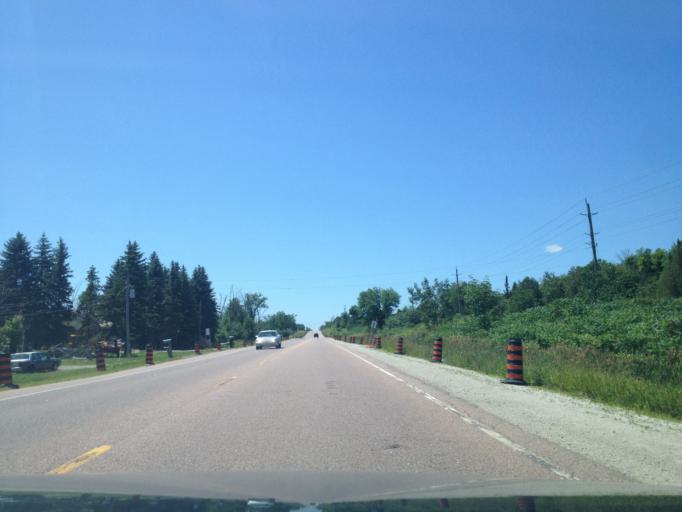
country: CA
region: Ontario
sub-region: Halton
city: Milton
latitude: 43.6684
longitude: -79.9939
